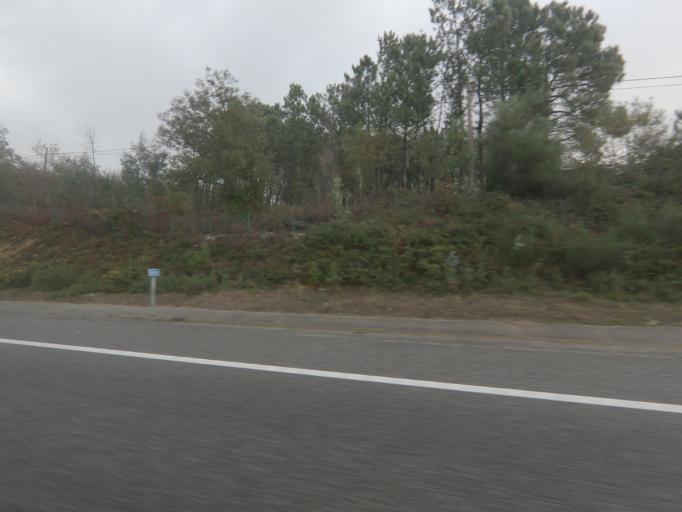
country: ES
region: Galicia
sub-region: Provincia de Pontevedra
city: Porrino
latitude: 42.1982
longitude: -8.6657
